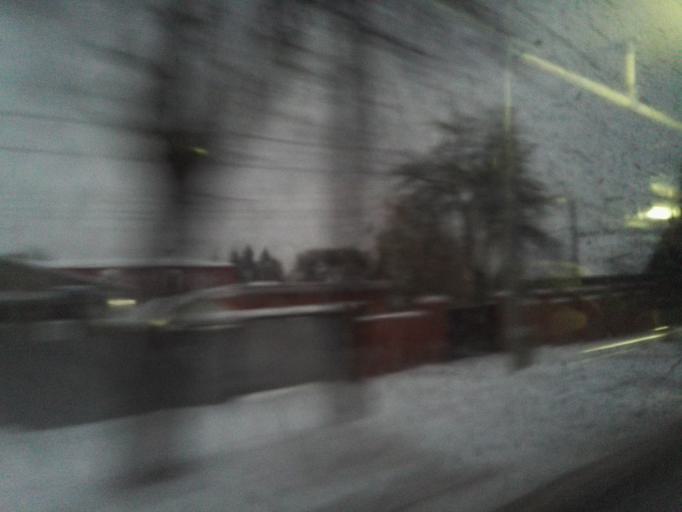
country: RU
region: Tula
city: Tula
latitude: 54.1673
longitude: 37.6048
